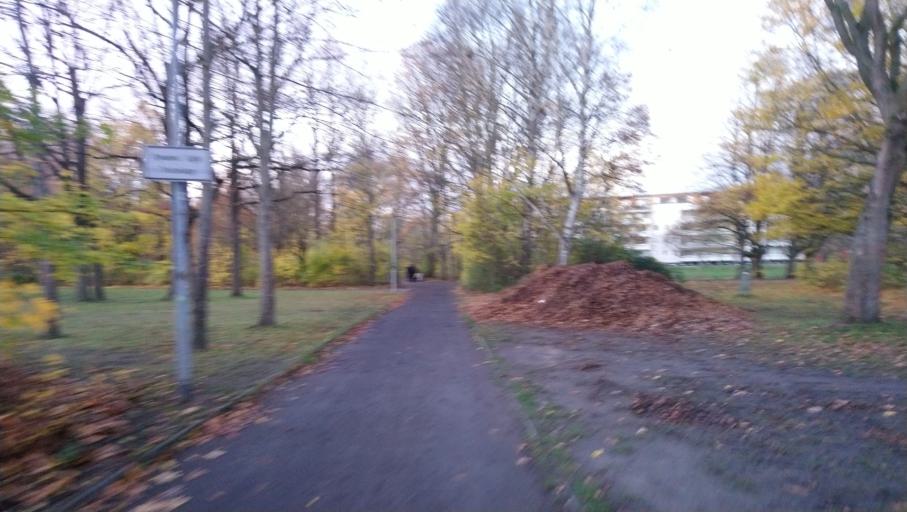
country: DE
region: Mecklenburg-Vorpommern
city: Rostock
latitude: 54.0675
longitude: 12.1192
